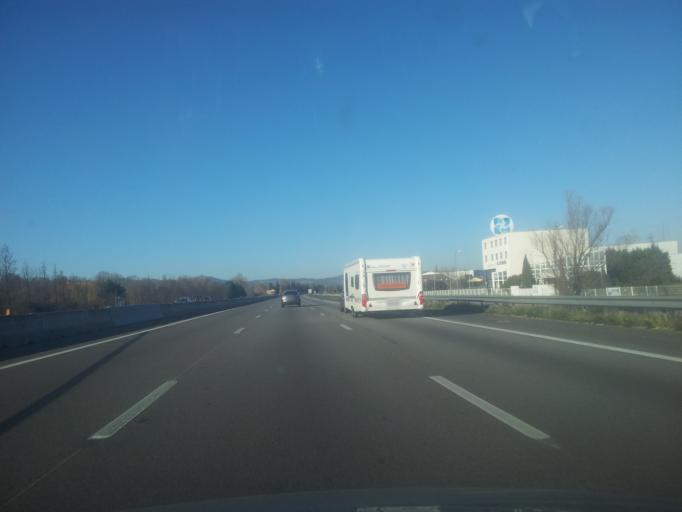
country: FR
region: Rhone-Alpes
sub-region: Departement de la Drome
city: Saulce-sur-Rhone
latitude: 44.6877
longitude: 4.7936
